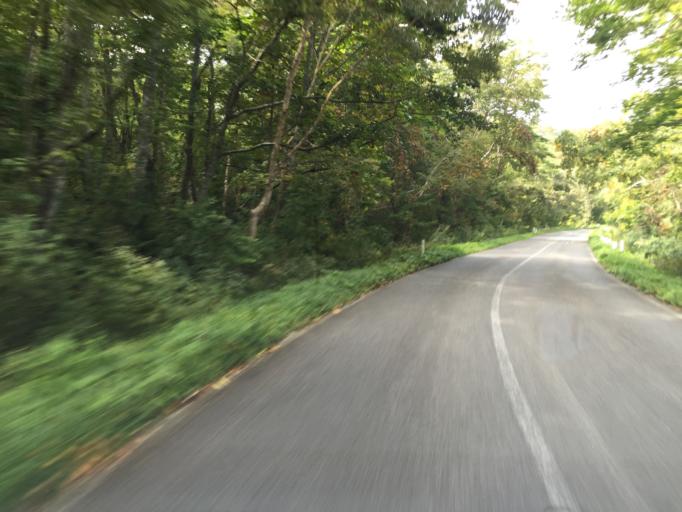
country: JP
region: Fukushima
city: Inawashiro
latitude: 37.6413
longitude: 140.0517
